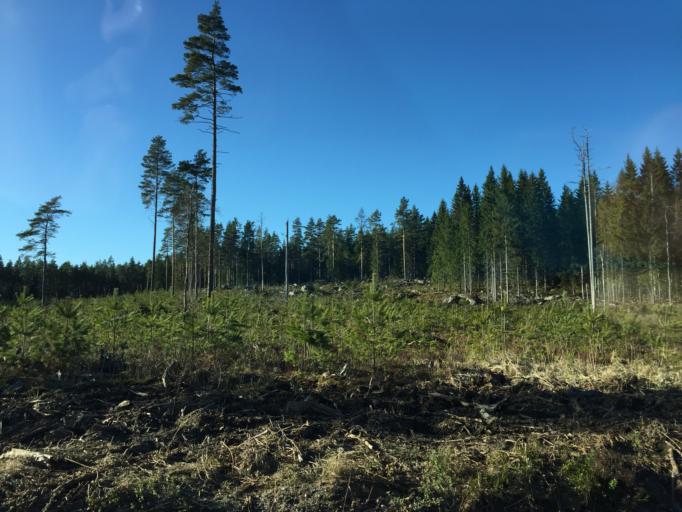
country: SE
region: Soedermanland
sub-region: Vingakers Kommun
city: Vingaker
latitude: 58.9564
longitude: 15.6718
